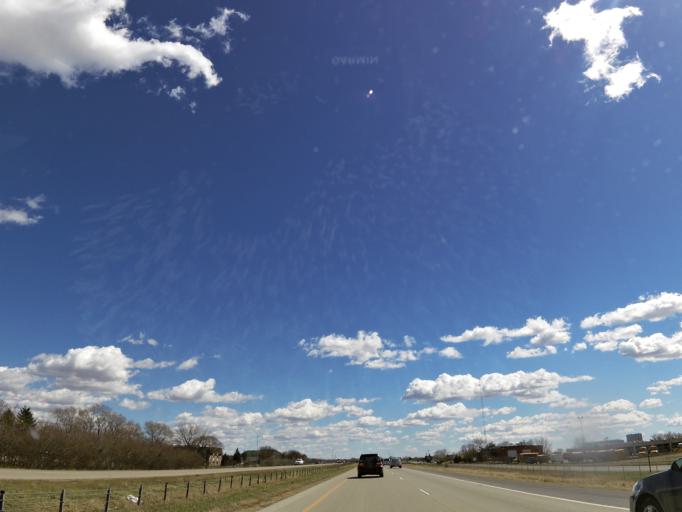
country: US
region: Minnesota
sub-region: Washington County
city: Cottage Grove
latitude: 44.8212
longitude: -92.9451
